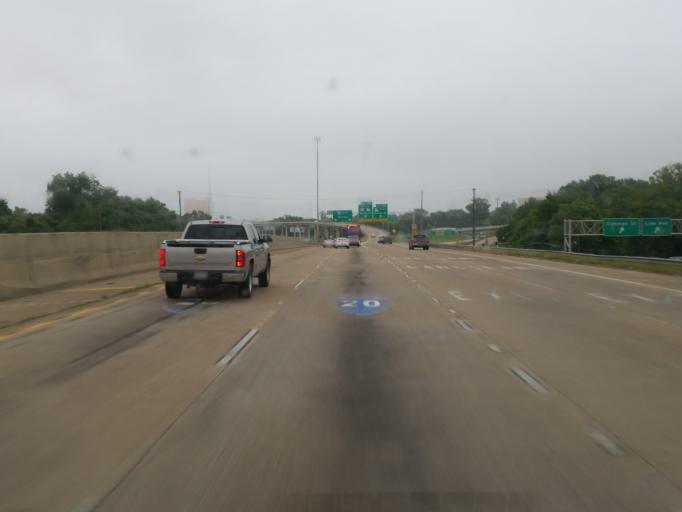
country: US
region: Louisiana
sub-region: Bossier Parish
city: Bossier City
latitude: 32.5011
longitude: -93.7505
